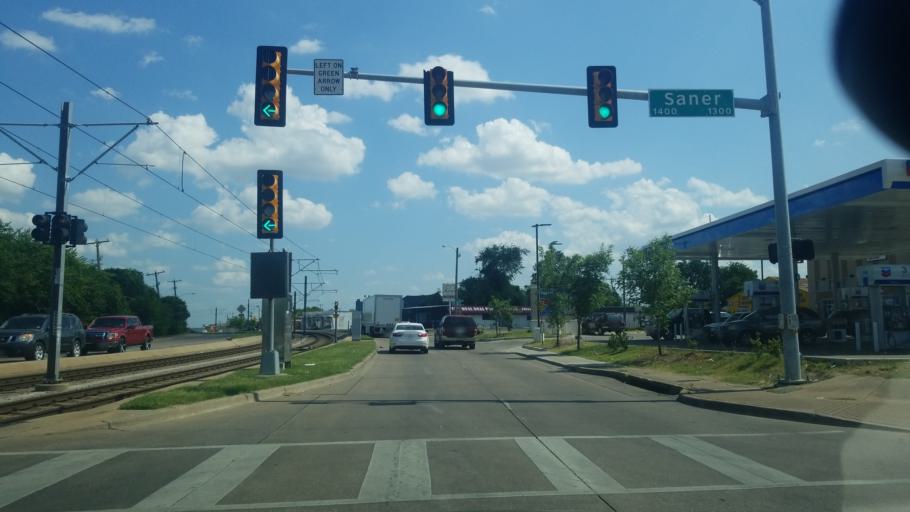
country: US
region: Texas
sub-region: Dallas County
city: Dallas
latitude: 32.7132
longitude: -96.8046
